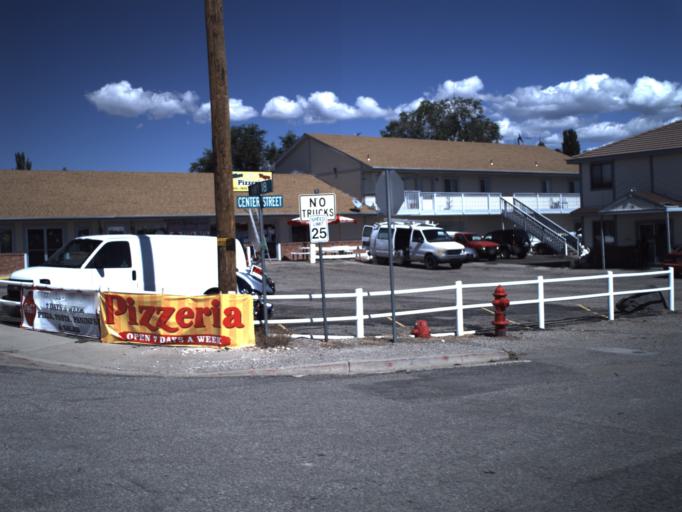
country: US
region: Utah
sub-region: Washington County
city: Ivins
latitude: 37.3379
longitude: -113.6932
